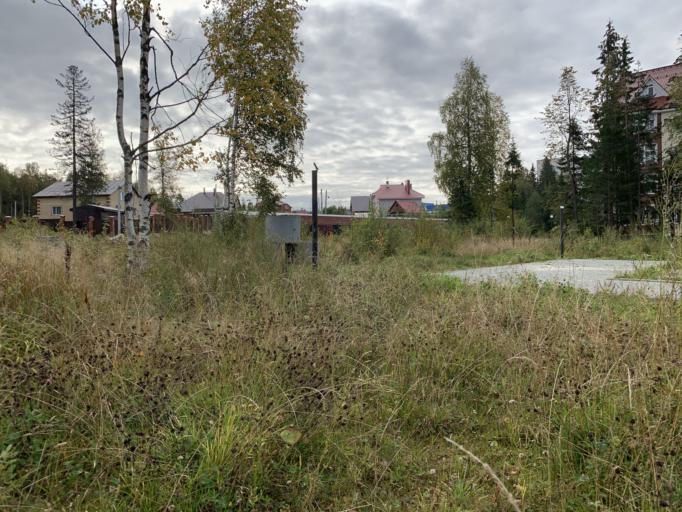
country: RU
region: Perm
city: Gubakha
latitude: 58.8310
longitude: 57.5597
